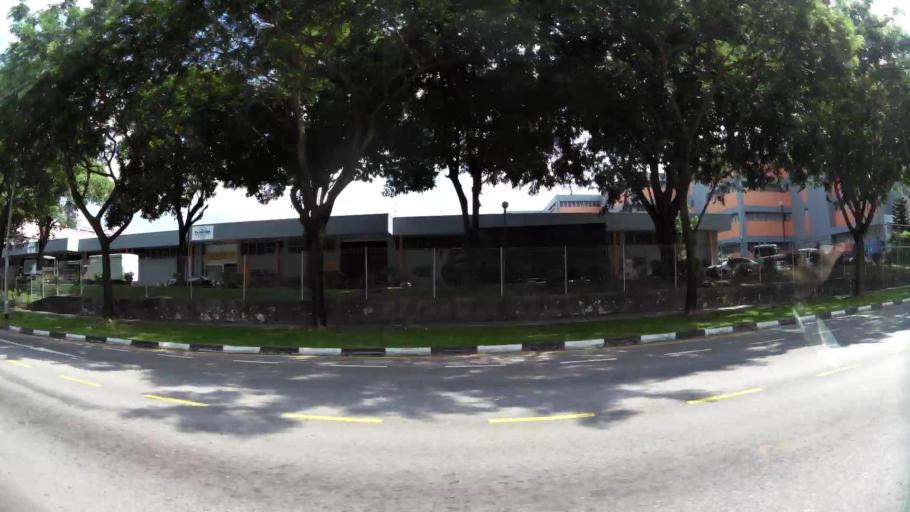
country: SG
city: Singapore
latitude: 1.3352
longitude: 103.8990
